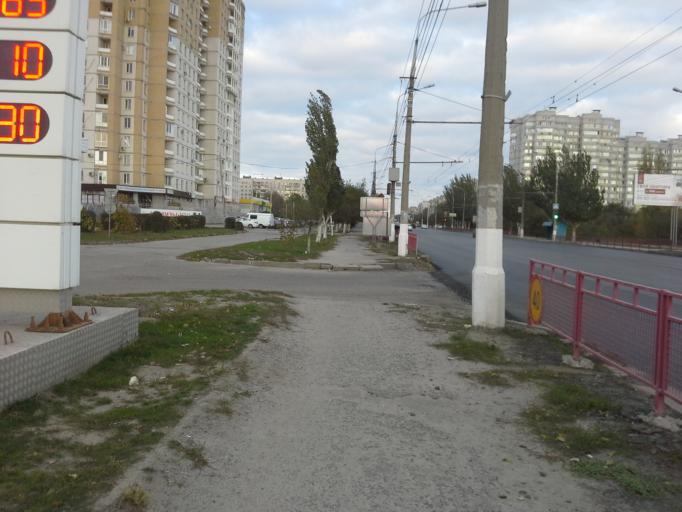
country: RU
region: Volgograd
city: Vodstroy
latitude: 48.8133
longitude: 44.6190
